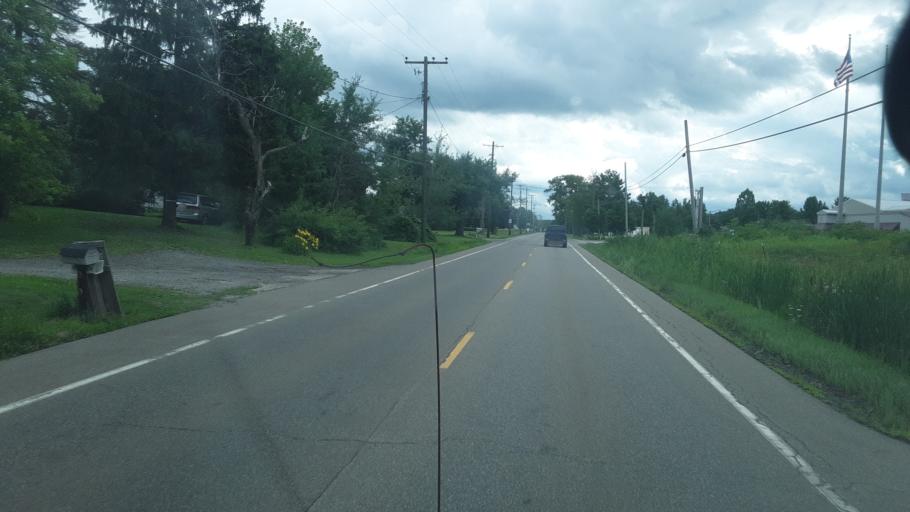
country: US
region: Ohio
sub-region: Ashtabula County
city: Jefferson
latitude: 41.7570
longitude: -80.7663
